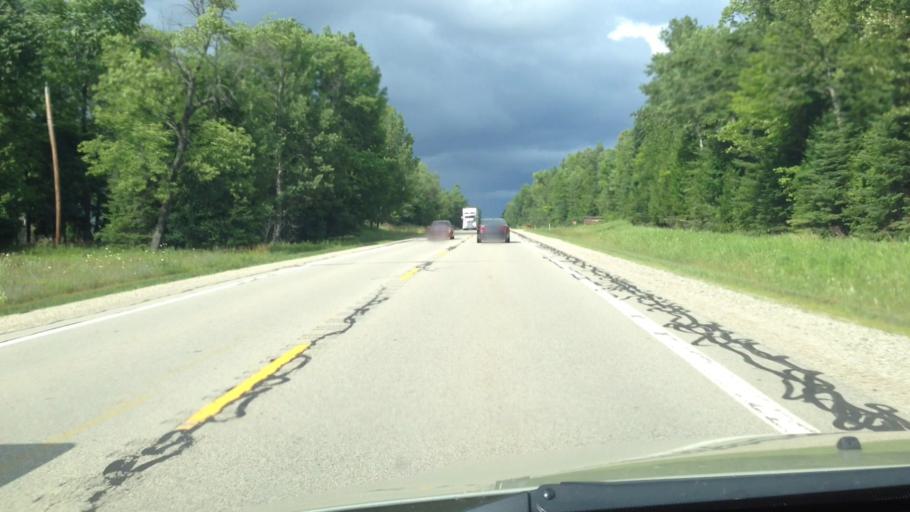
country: US
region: Michigan
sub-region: Menominee County
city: Menominee
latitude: 45.3415
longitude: -87.4137
